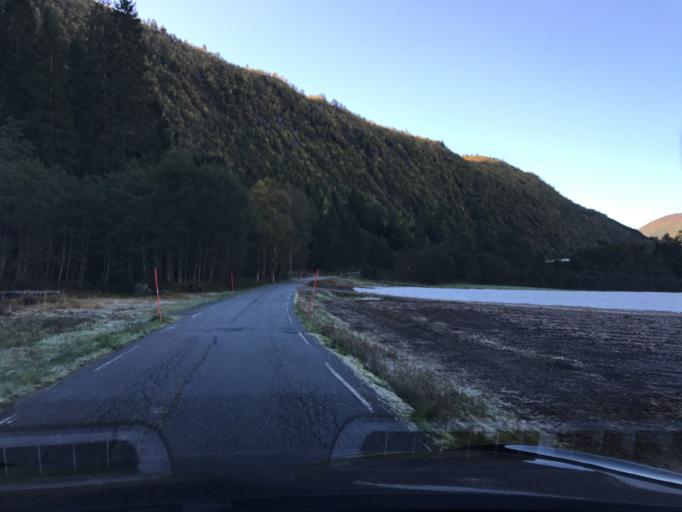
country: NO
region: More og Romsdal
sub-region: Norddal
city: Valldal
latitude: 62.3158
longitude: 7.3182
